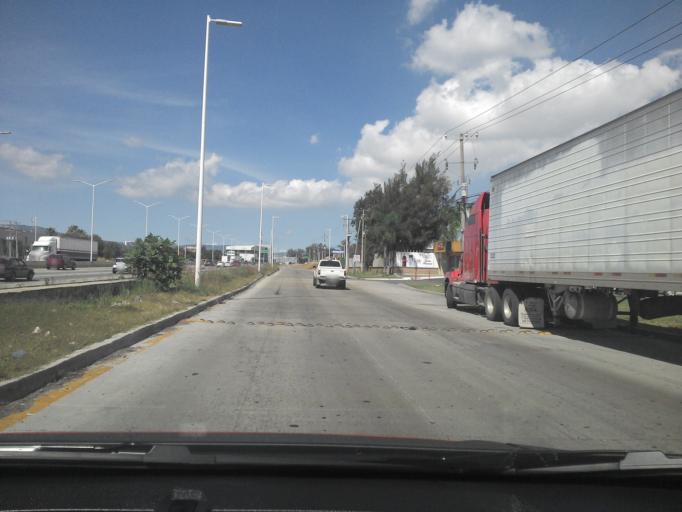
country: MX
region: Jalisco
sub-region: Tlajomulco de Zuniga
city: Altus Bosques
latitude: 20.5840
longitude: -103.3783
